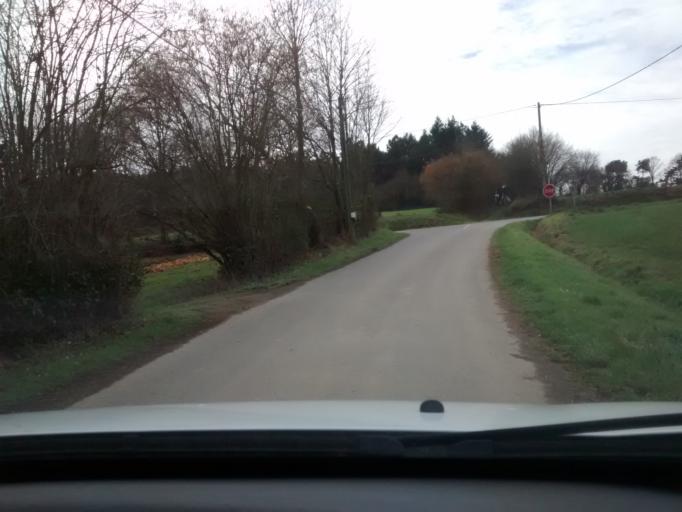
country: FR
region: Brittany
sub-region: Departement d'Ille-et-Vilaine
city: Liffre
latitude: 48.1997
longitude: -1.4768
